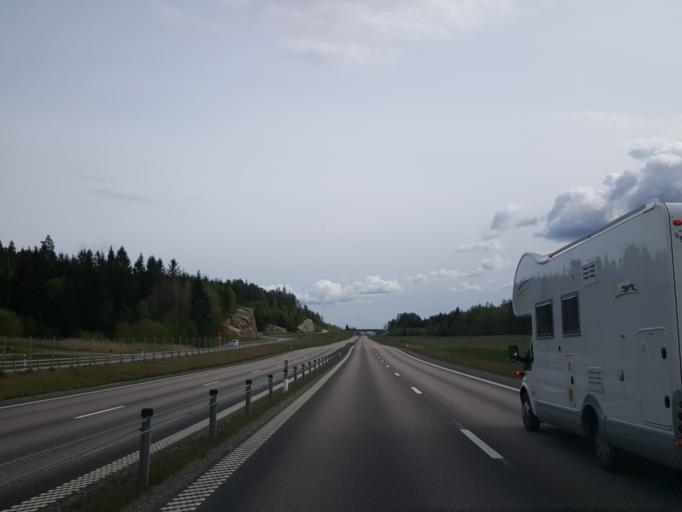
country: SE
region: Vaestra Goetaland
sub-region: Lilla Edets Kommun
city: Lilla Edet
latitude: 58.1780
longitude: 12.1407
